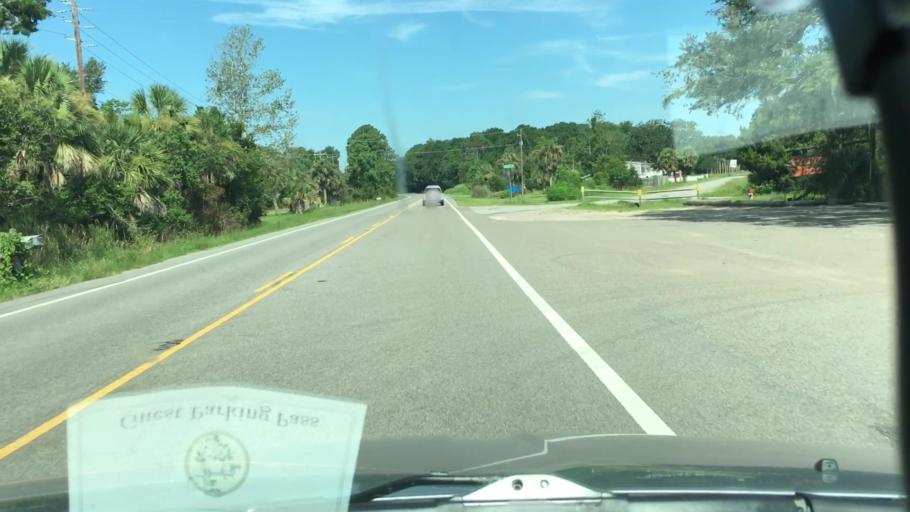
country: US
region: South Carolina
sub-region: Beaufort County
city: Beaufort
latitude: 32.4133
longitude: -80.4788
